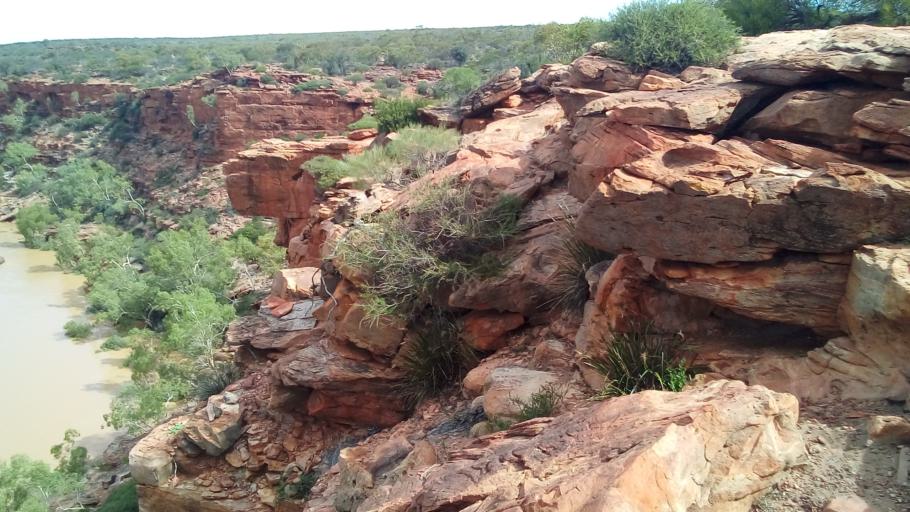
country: AU
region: Western Australia
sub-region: Northampton Shire
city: Kalbarri
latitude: -27.7890
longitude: 114.4685
